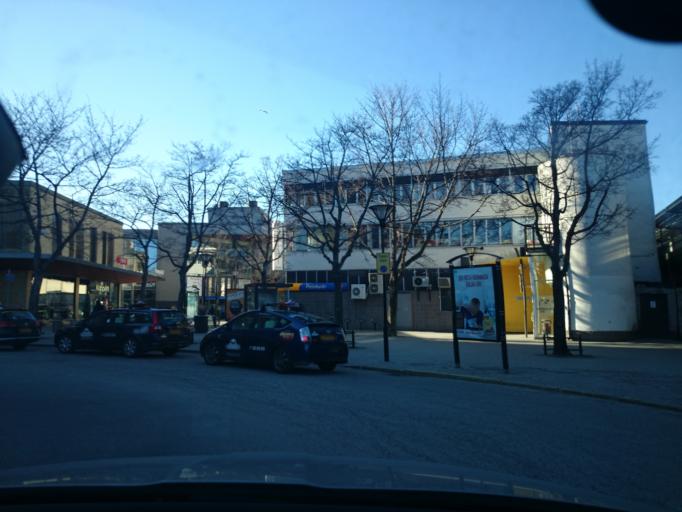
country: SE
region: Stockholm
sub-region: Stockholms Kommun
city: Arsta
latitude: 59.2431
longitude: 18.0940
